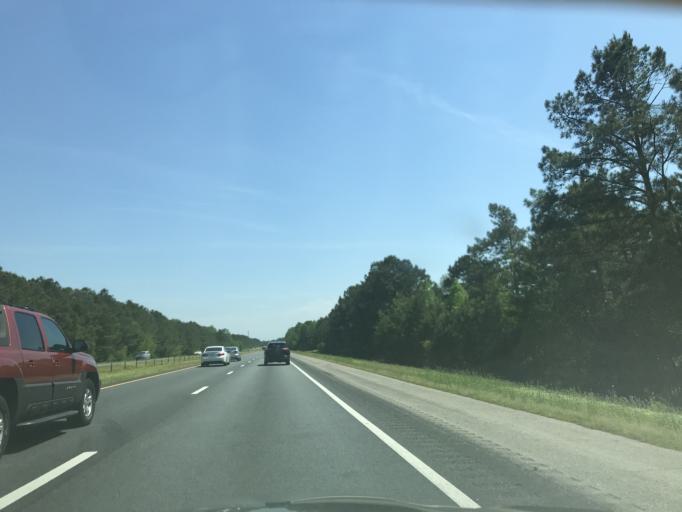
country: US
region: North Carolina
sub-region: Johnston County
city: Benson
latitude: 35.3614
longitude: -78.4881
